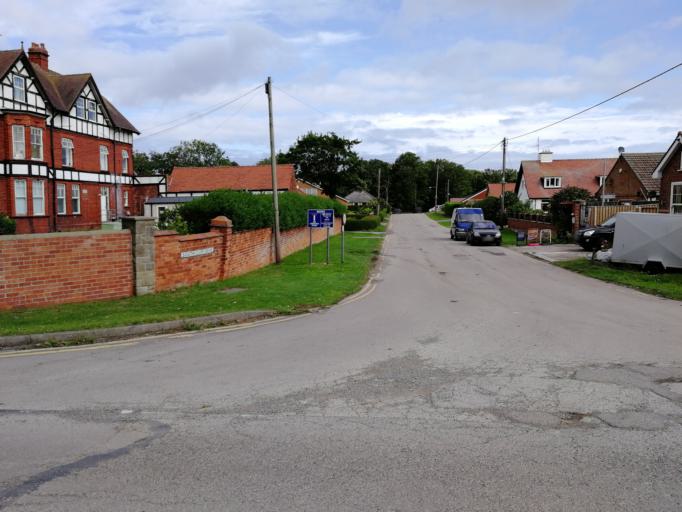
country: GB
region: England
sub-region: North Yorkshire
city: Filey
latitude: 54.1916
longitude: -0.2849
